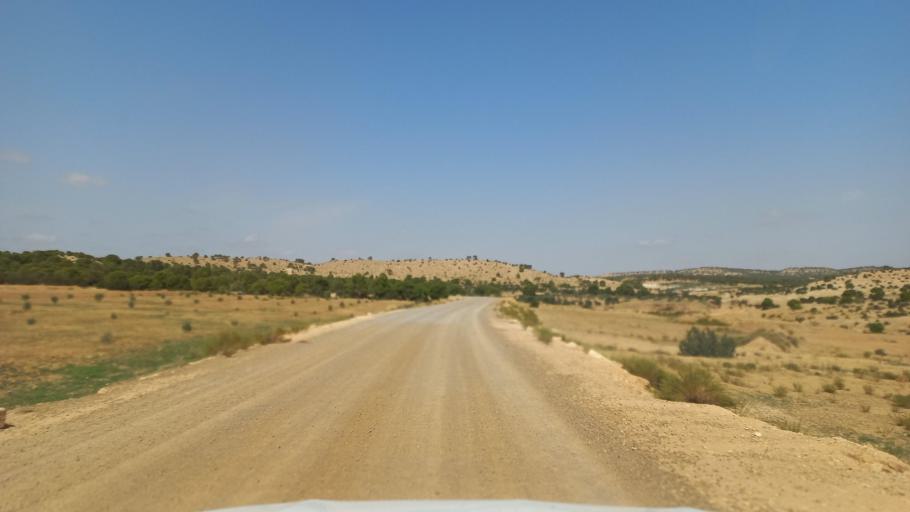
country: TN
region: Al Qasrayn
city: Sbiba
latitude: 35.3913
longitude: 8.9520
